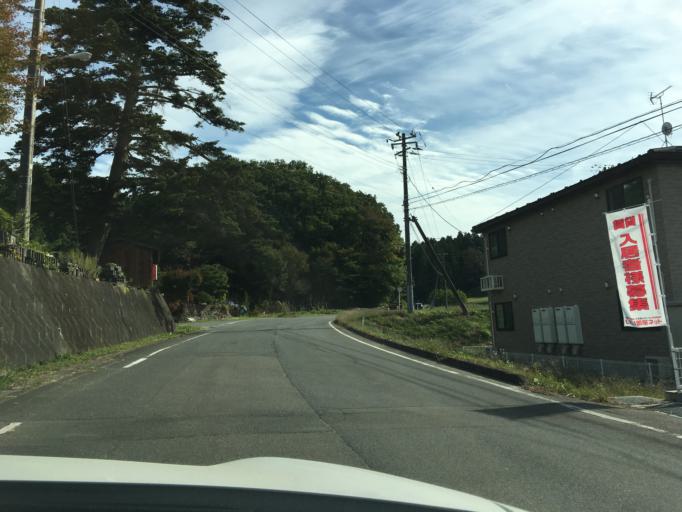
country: JP
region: Fukushima
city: Nihommatsu
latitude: 37.5891
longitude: 140.4633
